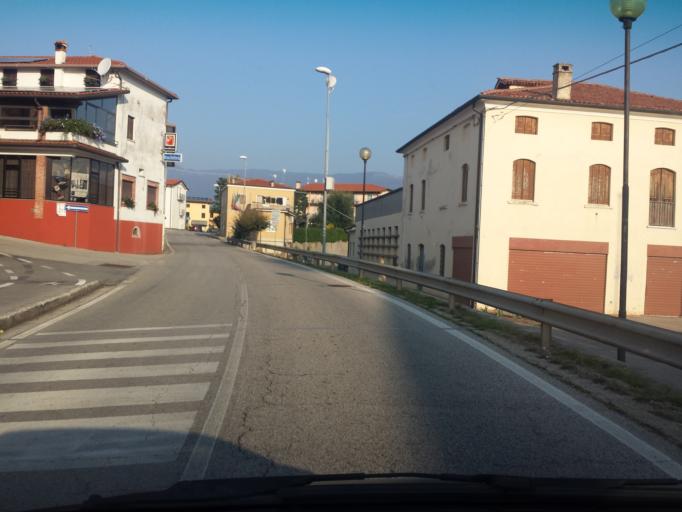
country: IT
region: Veneto
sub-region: Provincia di Vicenza
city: Mason Vicentino
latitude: 45.7308
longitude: 11.5838
